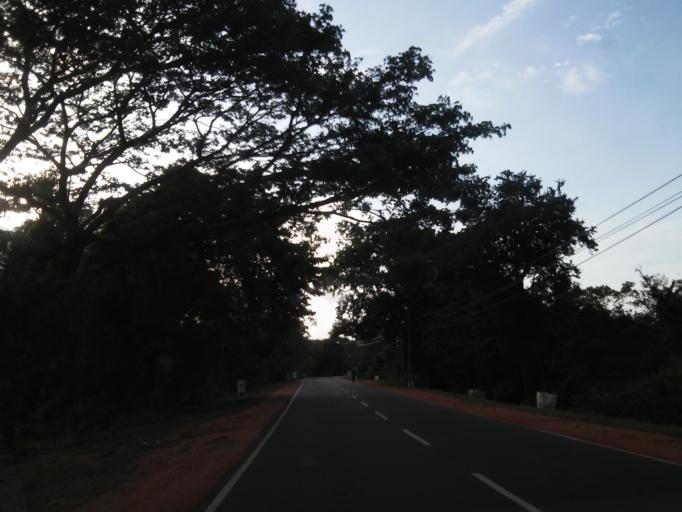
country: LK
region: Central
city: Sigiriya
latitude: 8.0922
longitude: 80.6314
